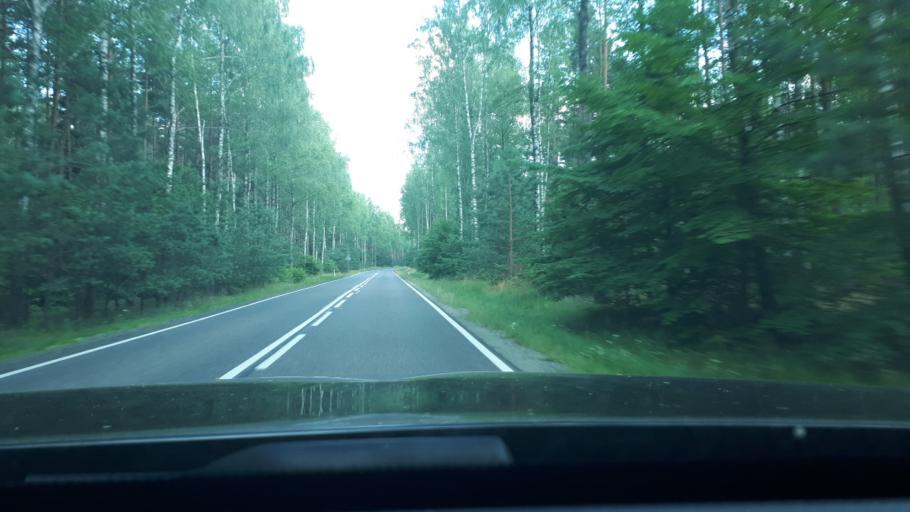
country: PL
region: Warmian-Masurian Voivodeship
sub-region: Powiat olsztynski
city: Stawiguda
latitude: 53.5334
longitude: 20.4345
